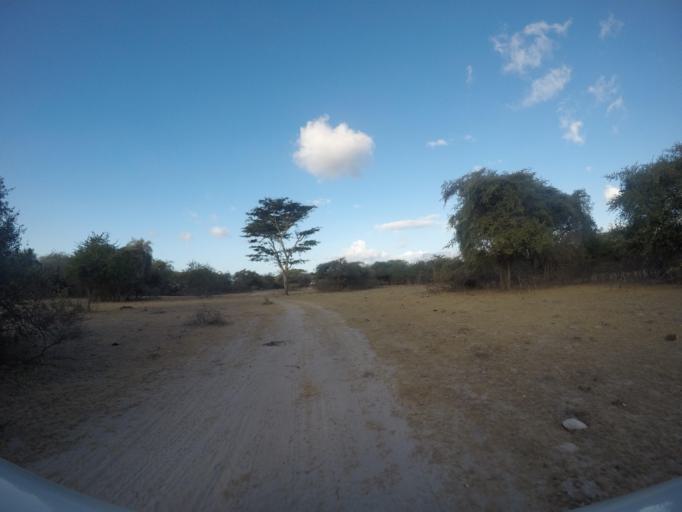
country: TL
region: Lautem
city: Lospalos
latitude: -8.3252
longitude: 126.9853
